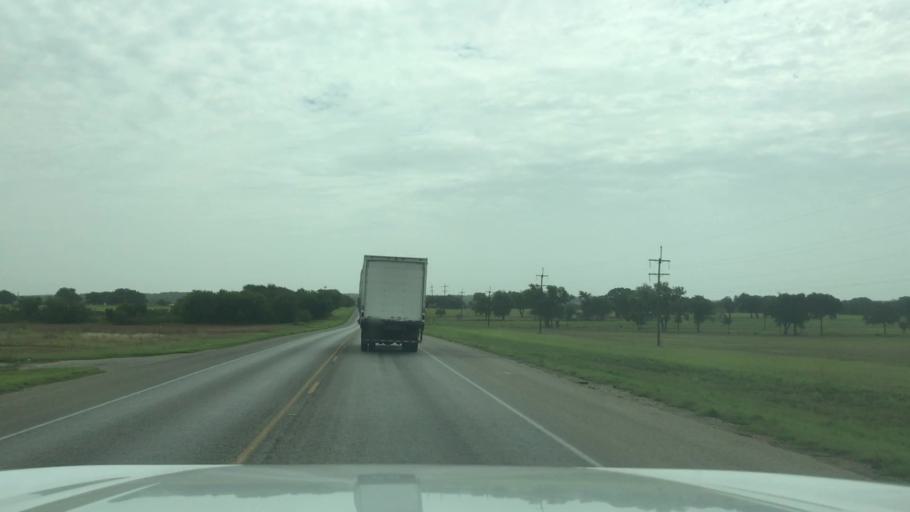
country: US
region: Texas
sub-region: Comanche County
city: De Leon
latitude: 32.0984
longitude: -98.4668
